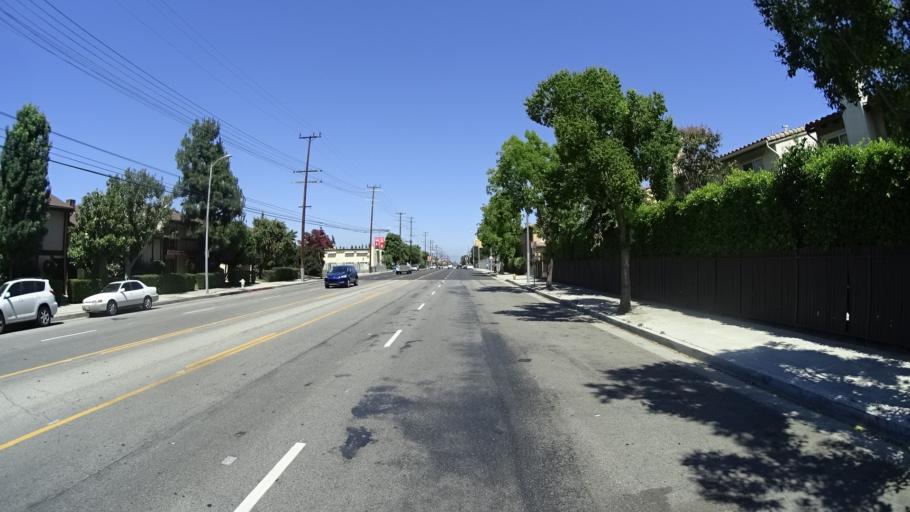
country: US
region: California
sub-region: Los Angeles County
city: Van Nuys
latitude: 34.1940
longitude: -118.4981
